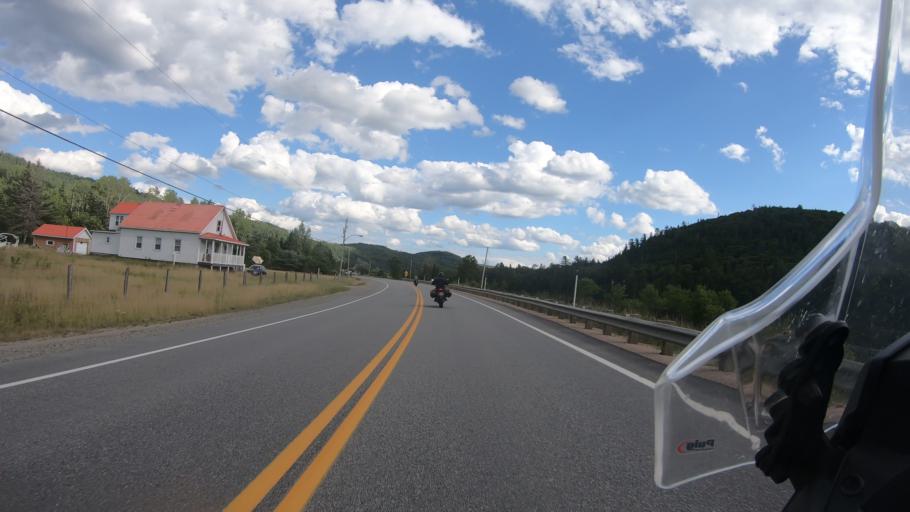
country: CA
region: Quebec
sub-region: Mauricie
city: Saint-Tite
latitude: 46.9863
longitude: -72.9108
